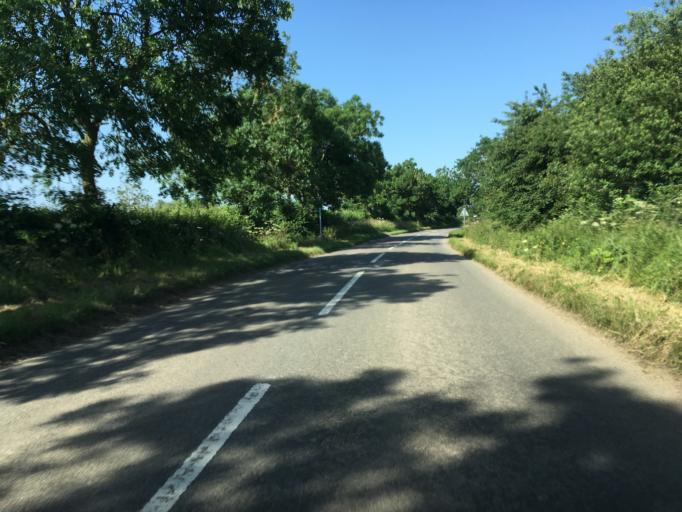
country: GB
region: England
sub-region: Buckinghamshire
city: Steeple Claydon
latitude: 51.9353
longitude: -1.0004
